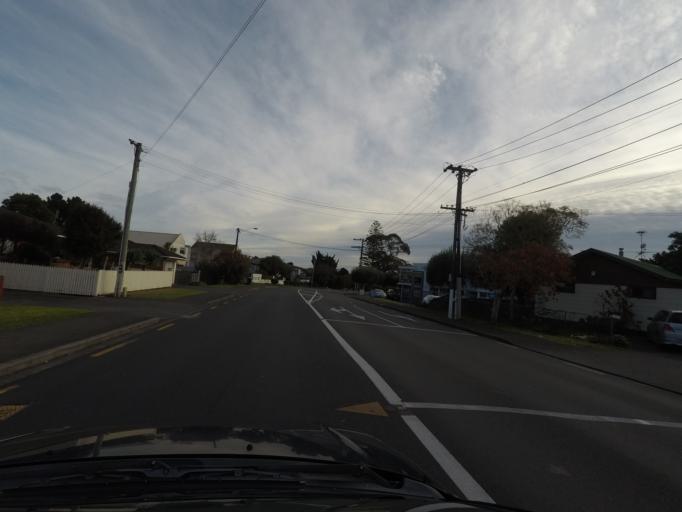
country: NZ
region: Auckland
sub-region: Auckland
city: Tamaki
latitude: -36.8946
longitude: 174.8392
